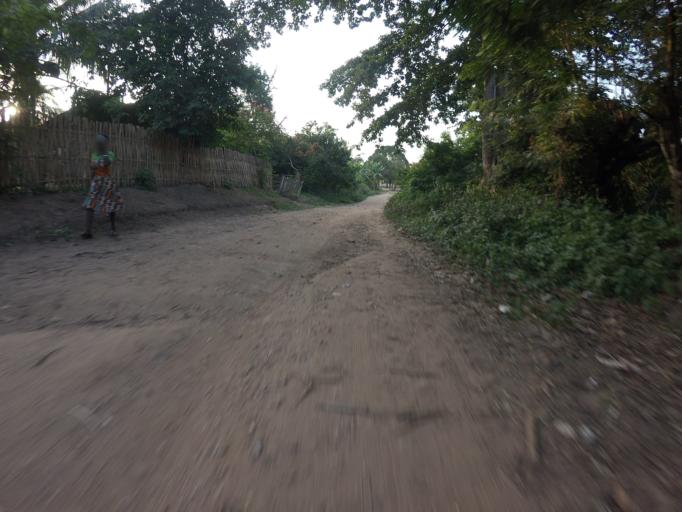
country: GH
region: Volta
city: Kpandu
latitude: 6.8913
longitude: 0.4340
